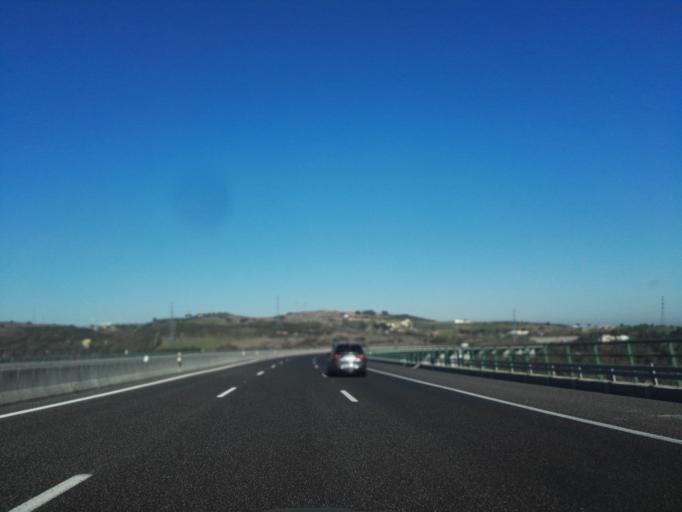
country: PT
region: Lisbon
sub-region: Vila Franca de Xira
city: Sobralinho
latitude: 38.9315
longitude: -9.0739
